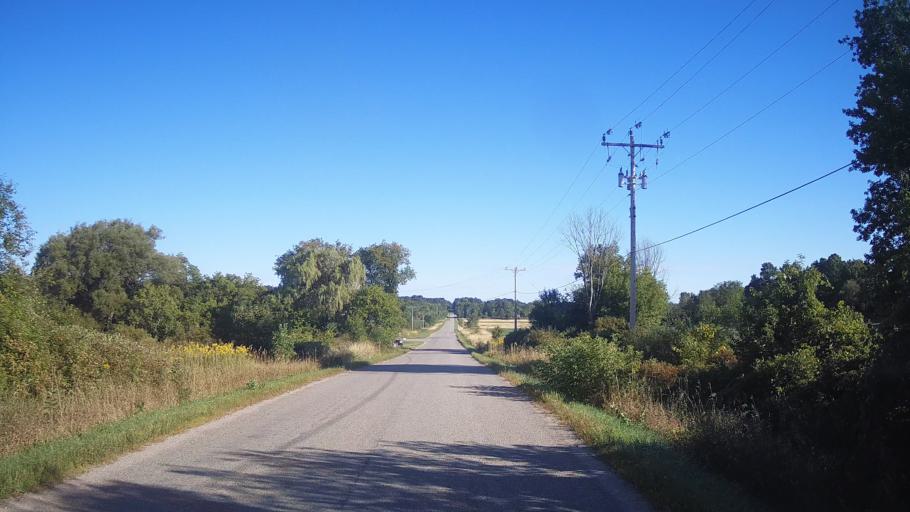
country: US
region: New York
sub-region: Jefferson County
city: Alexandria Bay
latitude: 44.4322
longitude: -75.9811
